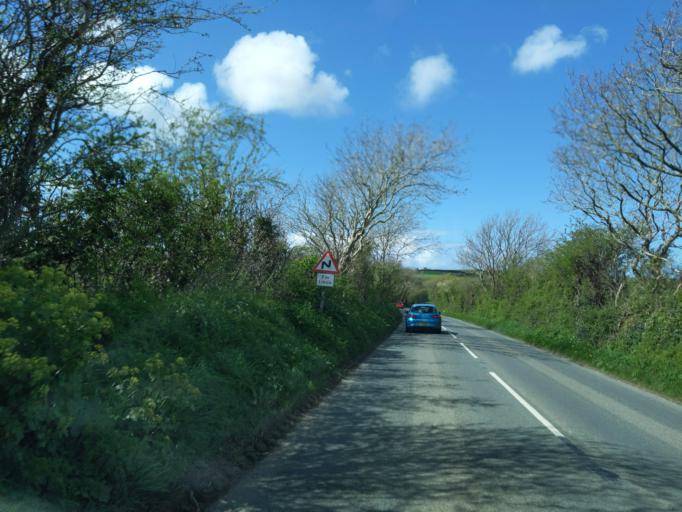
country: GB
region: England
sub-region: Cornwall
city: Wadebridge
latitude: 50.5391
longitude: -4.8544
